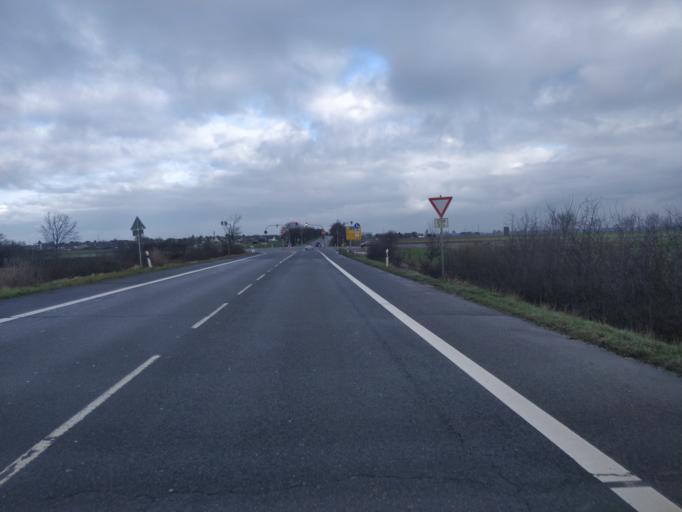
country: DE
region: North Rhine-Westphalia
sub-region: Regierungsbezirk Koln
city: Euskirchen
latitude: 50.6500
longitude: 6.8413
